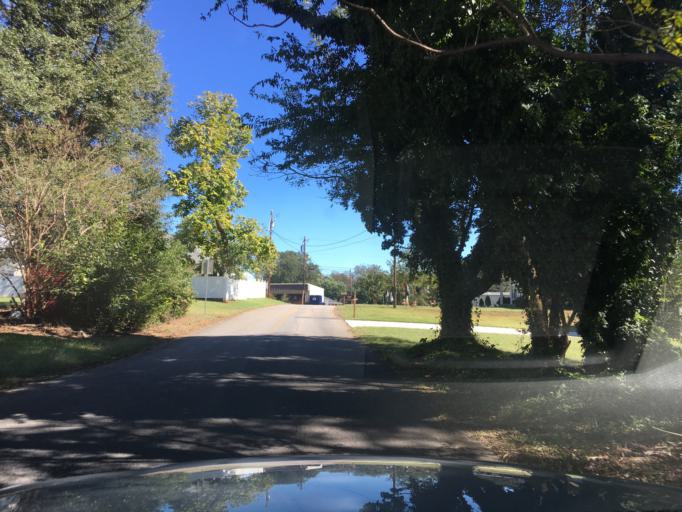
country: US
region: South Carolina
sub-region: Spartanburg County
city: Duncan
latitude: 34.9371
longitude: -82.1408
